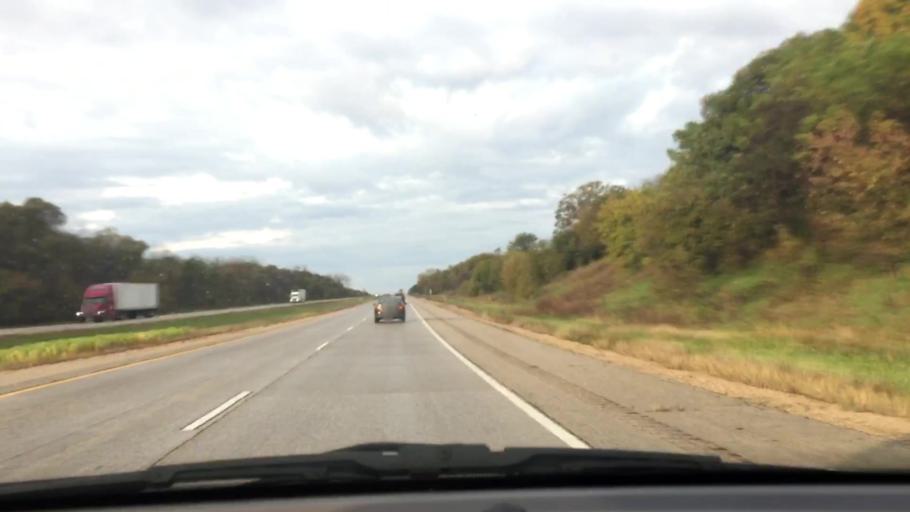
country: US
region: Wisconsin
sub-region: Walworth County
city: Darien
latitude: 42.5829
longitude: -88.7662
